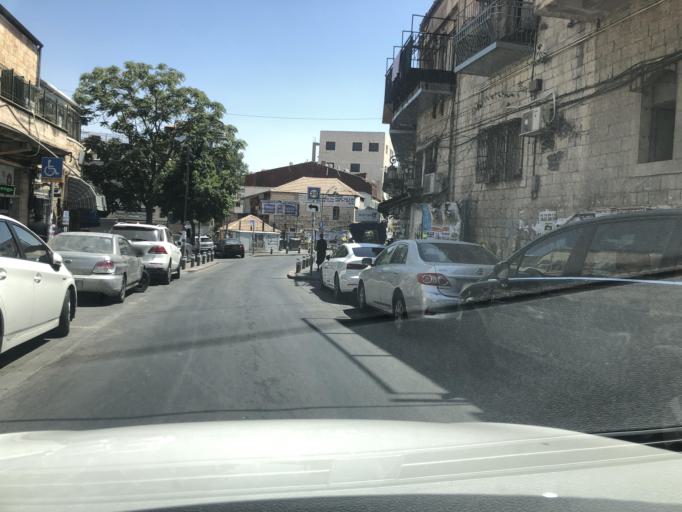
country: IL
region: Jerusalem
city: West Jerusalem
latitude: 31.7880
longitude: 35.2202
